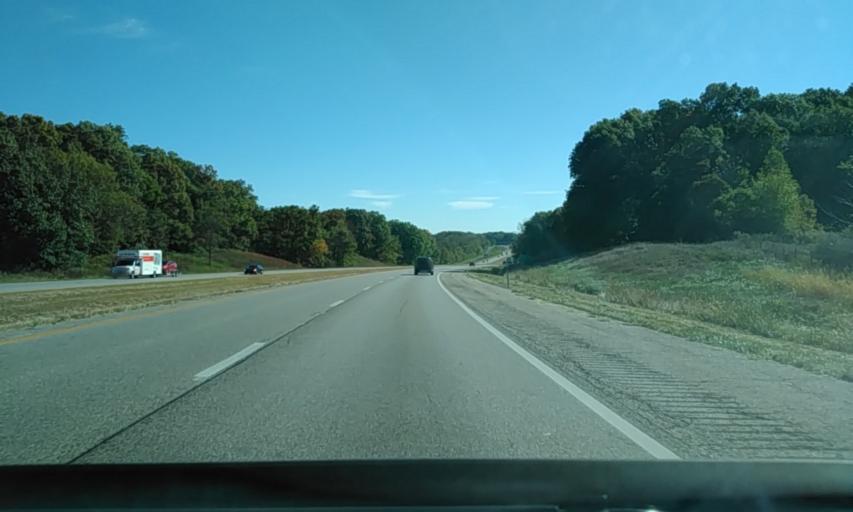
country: US
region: Illinois
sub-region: Bond County
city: Greenville
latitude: 38.8346
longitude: -89.5328
